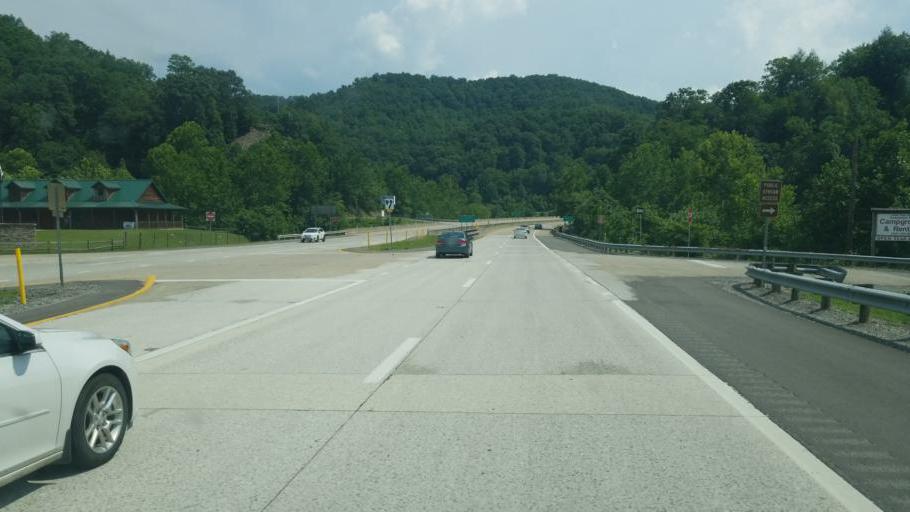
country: US
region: West Virginia
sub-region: Kanawha County
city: Alum Creek
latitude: 38.1838
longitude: -81.8501
